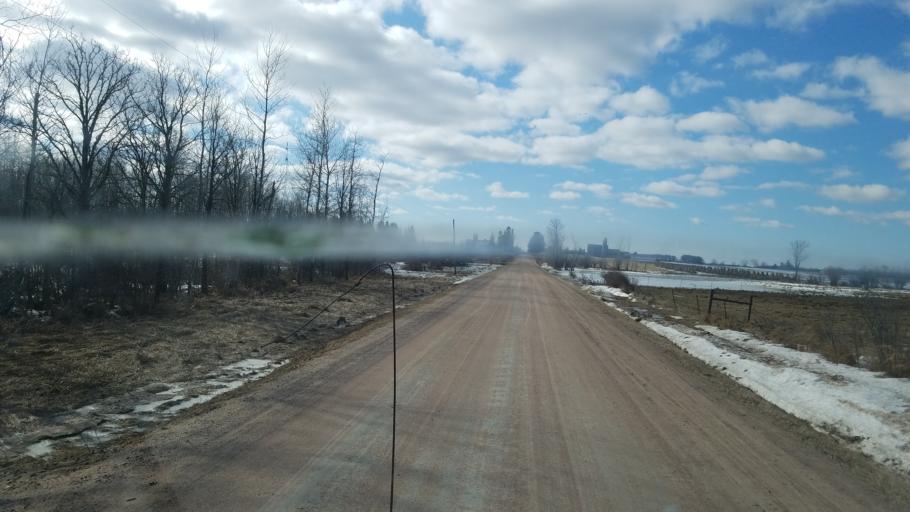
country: US
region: Wisconsin
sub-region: Clark County
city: Loyal
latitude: 44.6538
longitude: -90.3978
